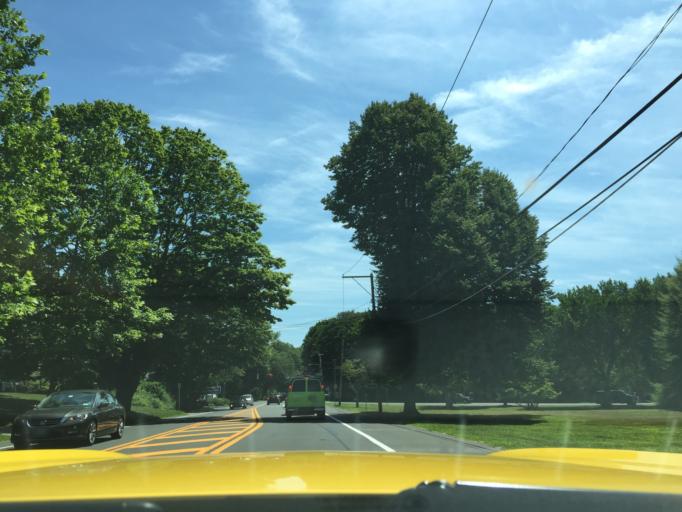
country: US
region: New York
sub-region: Suffolk County
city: East Hampton
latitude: 40.9545
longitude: -72.2050
